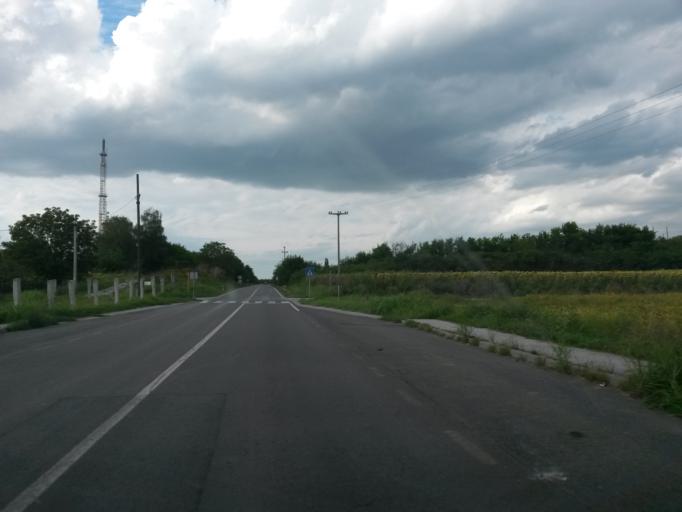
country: HR
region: Vukovarsko-Srijemska
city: Jarmina
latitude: 45.3010
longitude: 18.7367
